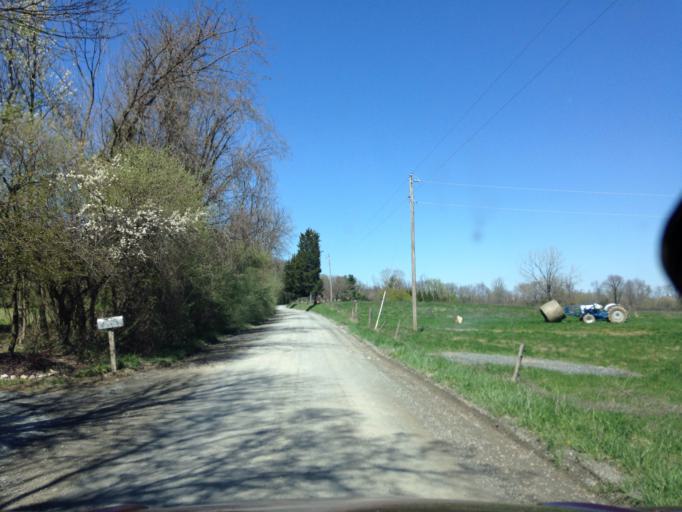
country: US
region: Virginia
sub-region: Loudoun County
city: Lovettsville
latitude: 39.2846
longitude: -77.5950
